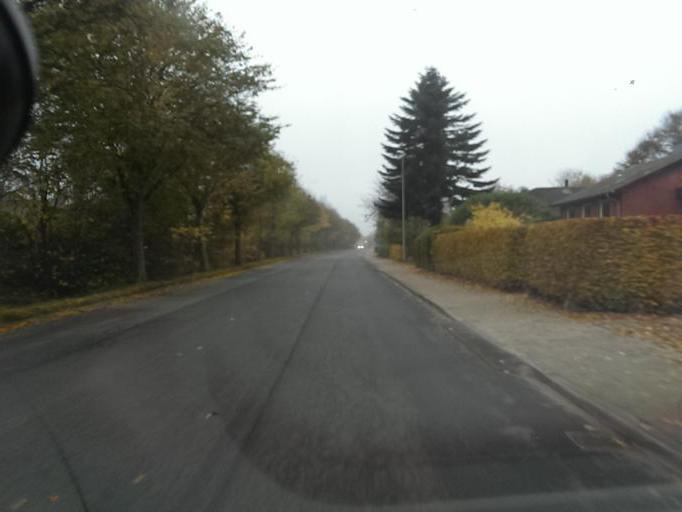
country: DK
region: South Denmark
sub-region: Esbjerg Kommune
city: Bramming
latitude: 55.4653
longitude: 8.7144
